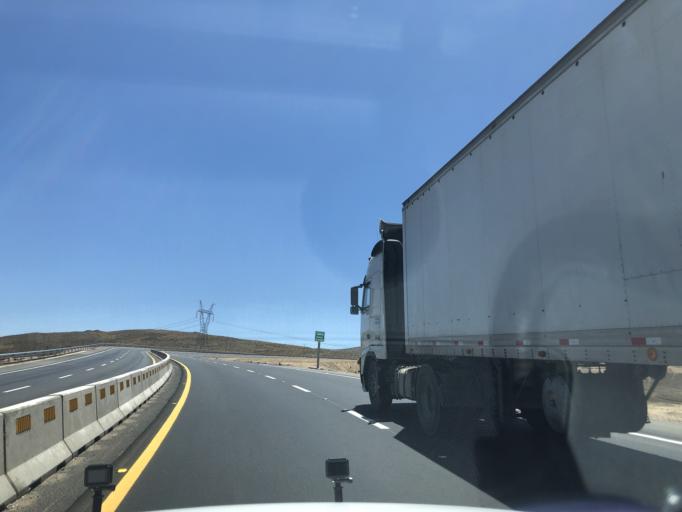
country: BO
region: Cochabamba
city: Colchani
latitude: -17.6861
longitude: -66.7537
